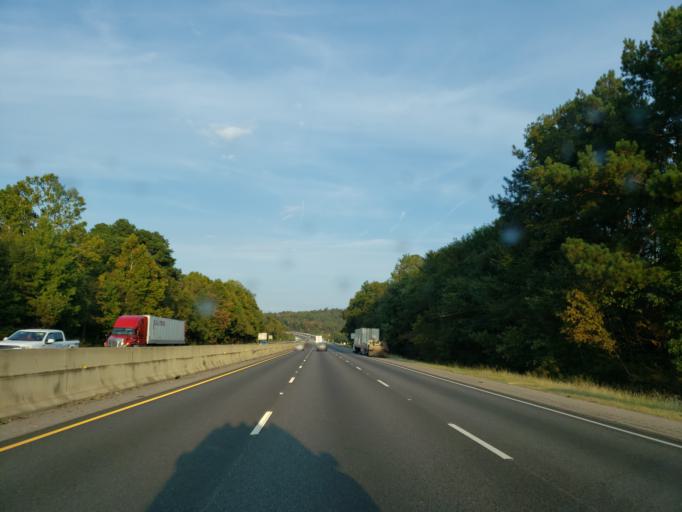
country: US
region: Alabama
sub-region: Saint Clair County
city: Moody
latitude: 33.5791
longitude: -86.4678
